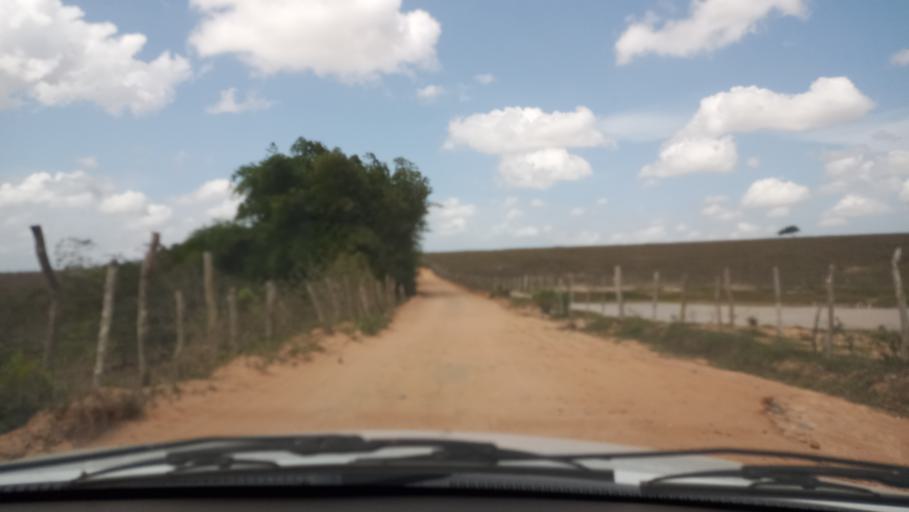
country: BR
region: Rio Grande do Norte
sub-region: Montanhas
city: Montanhas
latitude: -6.3558
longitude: -35.3363
